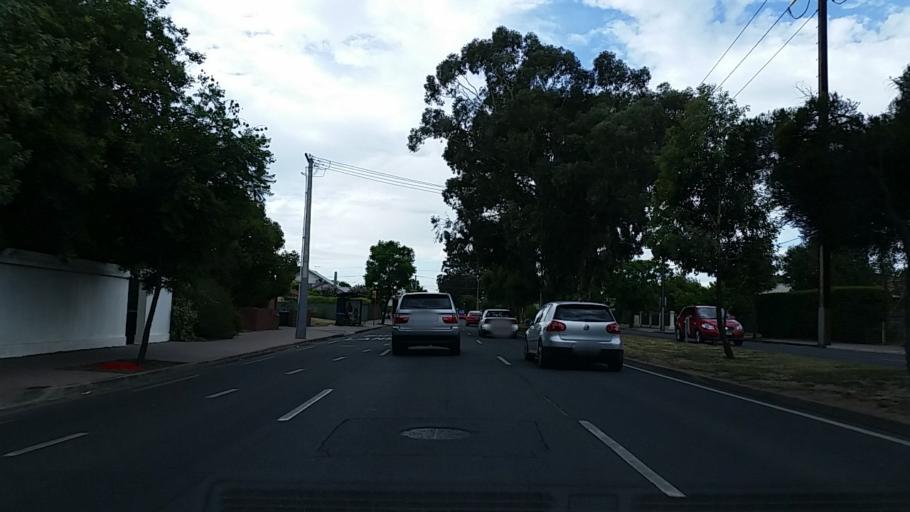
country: AU
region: South Australia
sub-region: Mitcham
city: Clapham
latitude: -34.9887
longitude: 138.5924
